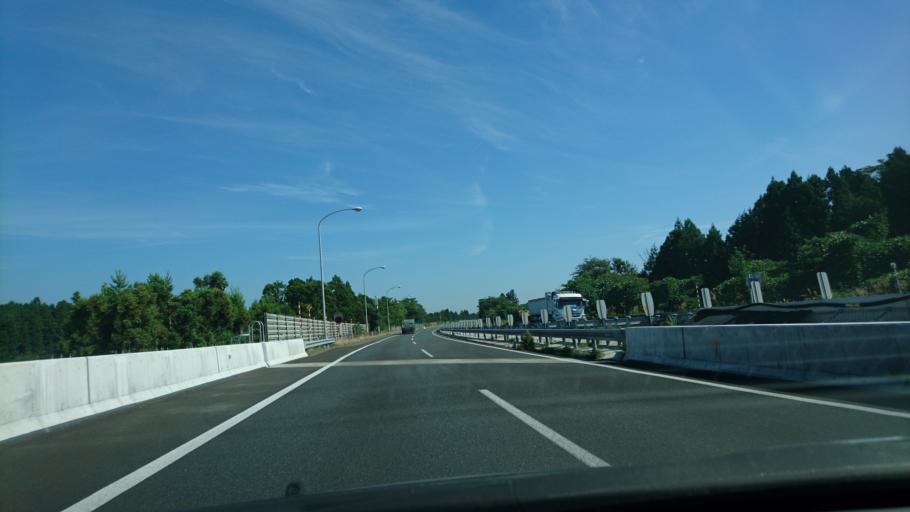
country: JP
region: Iwate
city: Mizusawa
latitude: 39.0744
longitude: 141.0998
